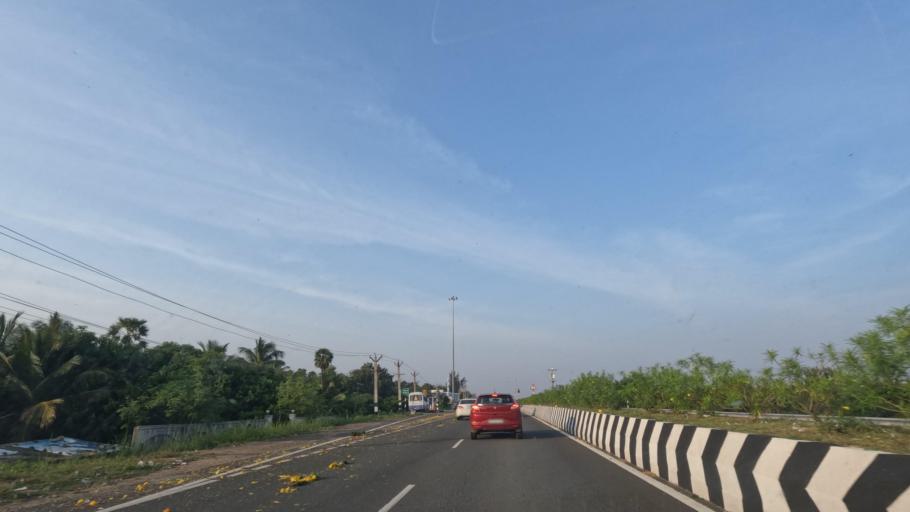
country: IN
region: Tamil Nadu
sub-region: Kancheepuram
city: Mamallapuram
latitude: 12.7254
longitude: 80.2310
